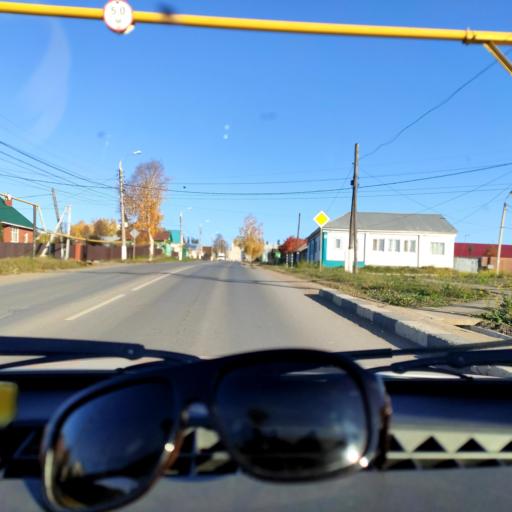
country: RU
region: Bashkortostan
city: Blagoveshchensk
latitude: 55.0420
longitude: 55.9611
